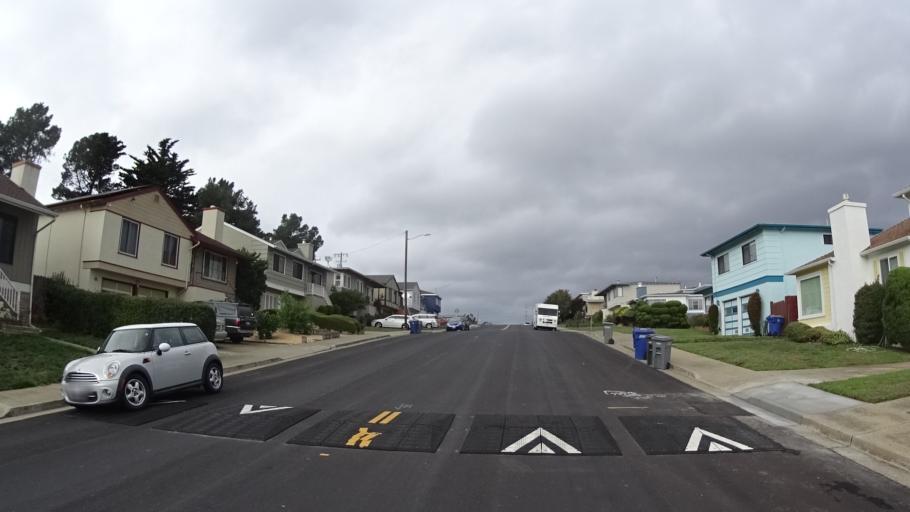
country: US
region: California
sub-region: San Mateo County
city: San Bruno
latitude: 37.6394
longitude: -122.4401
